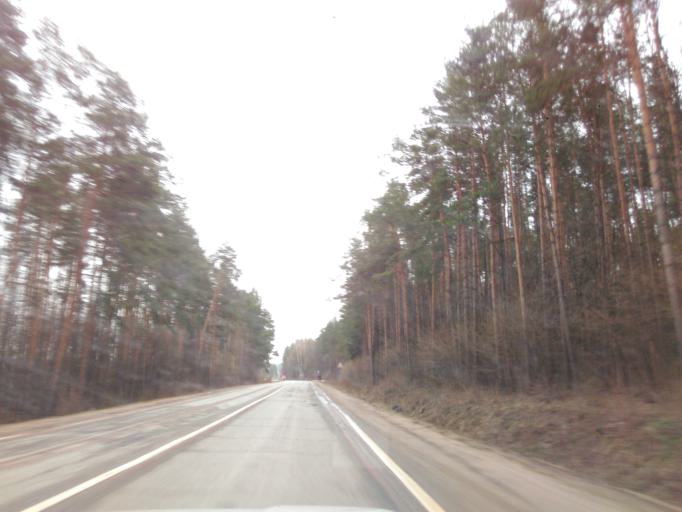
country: RU
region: Moskovskaya
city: Snegiri
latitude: 55.8524
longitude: 36.9428
